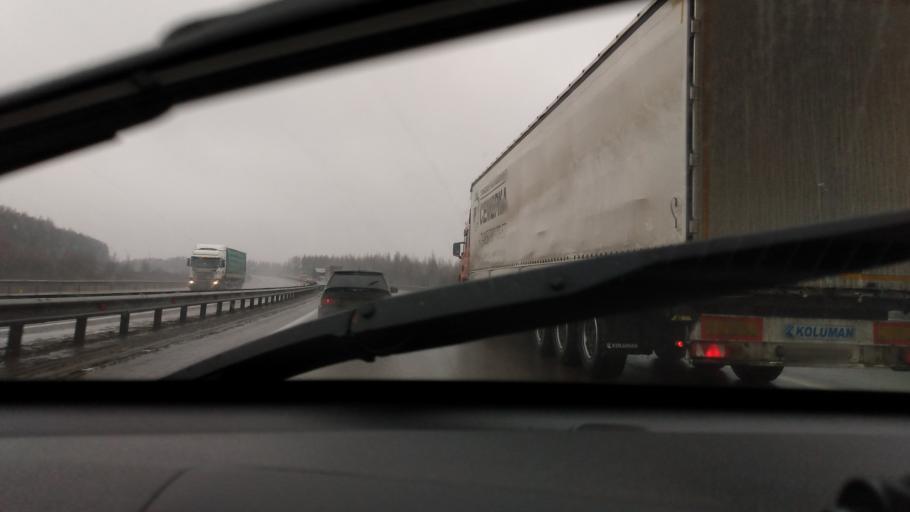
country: RU
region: Tula
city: Shvartsevskiy
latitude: 54.0897
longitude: 38.0421
